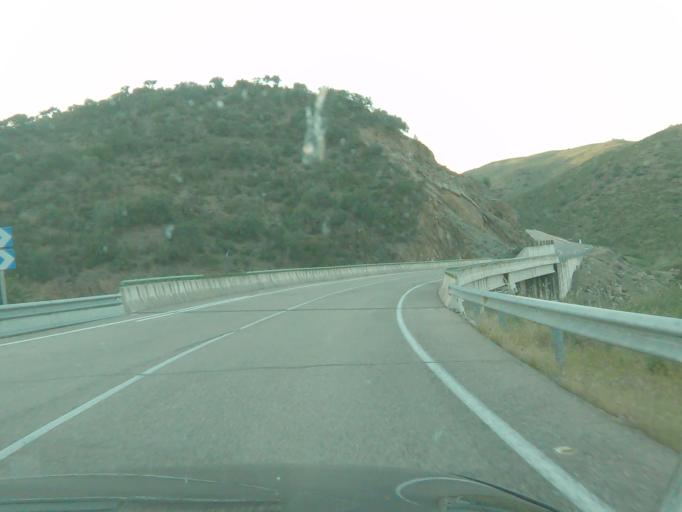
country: ES
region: Extremadura
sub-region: Provincia de Caceres
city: Salorino
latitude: 39.5709
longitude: -6.9983
